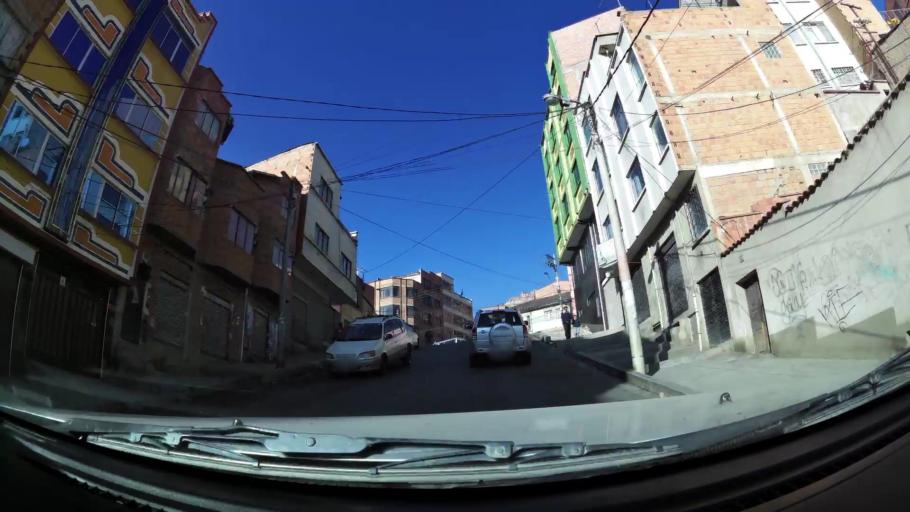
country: BO
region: La Paz
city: La Paz
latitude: -16.5041
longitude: -68.1436
